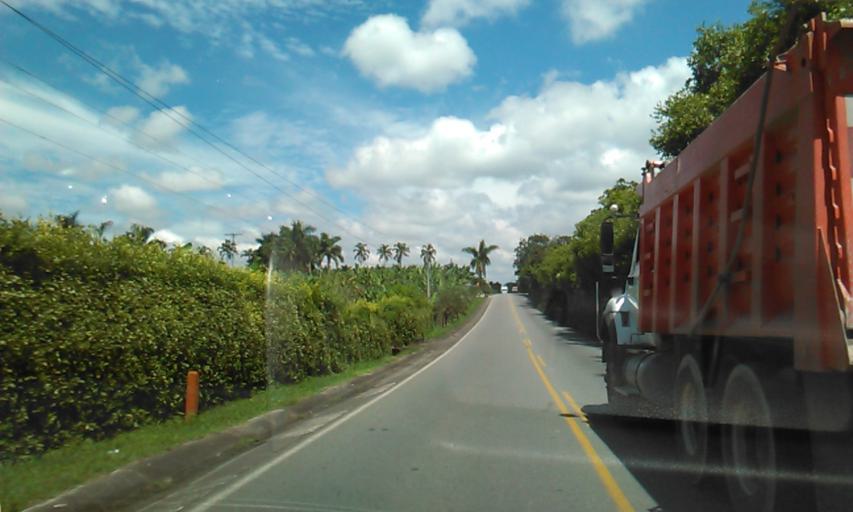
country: CO
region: Quindio
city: Armenia
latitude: 4.4705
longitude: -75.7040
